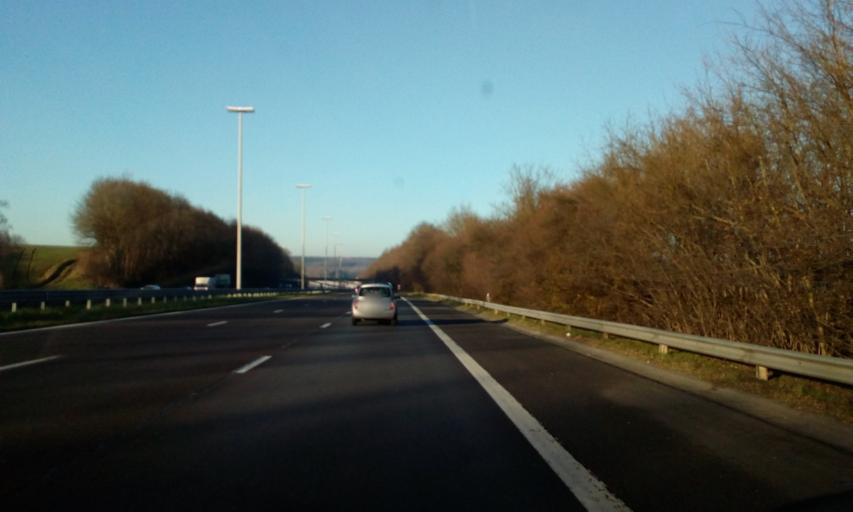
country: BE
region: Wallonia
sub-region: Province du Brabant Wallon
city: Braine-le-Chateau
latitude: 50.6759
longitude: 4.3100
